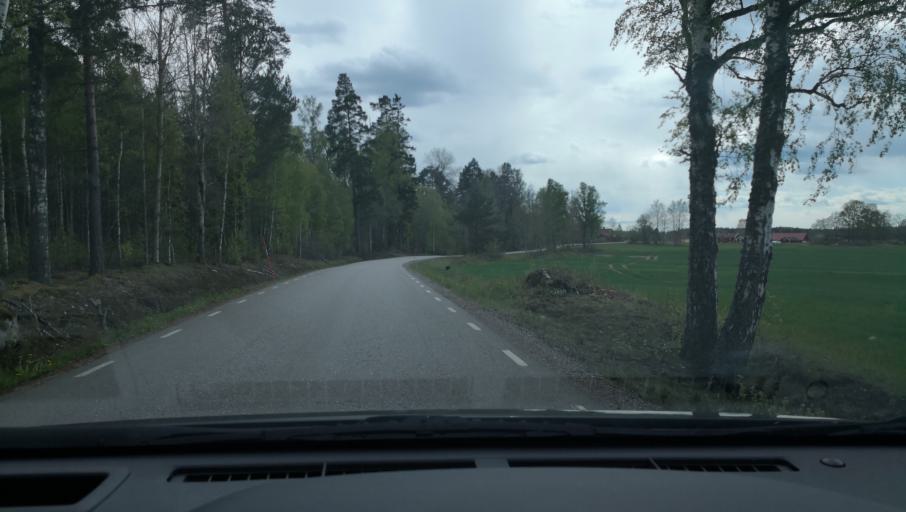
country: SE
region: OErebro
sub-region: Kumla Kommun
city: Kumla
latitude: 59.1543
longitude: 15.1766
